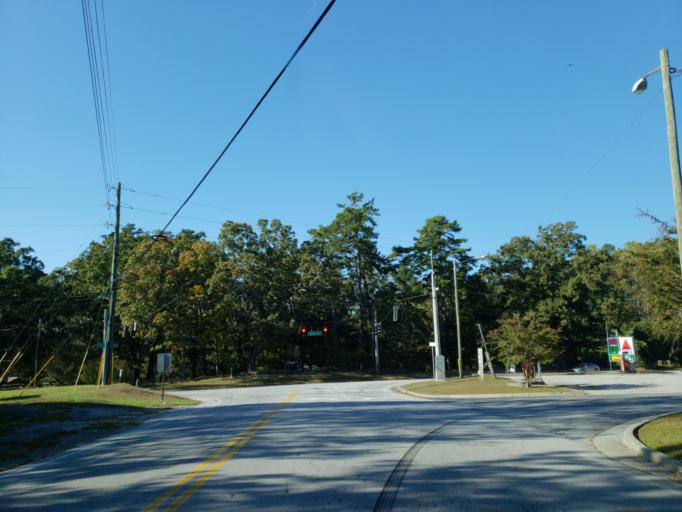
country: US
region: Georgia
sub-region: Gwinnett County
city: Lawrenceville
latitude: 33.9946
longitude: -83.9765
